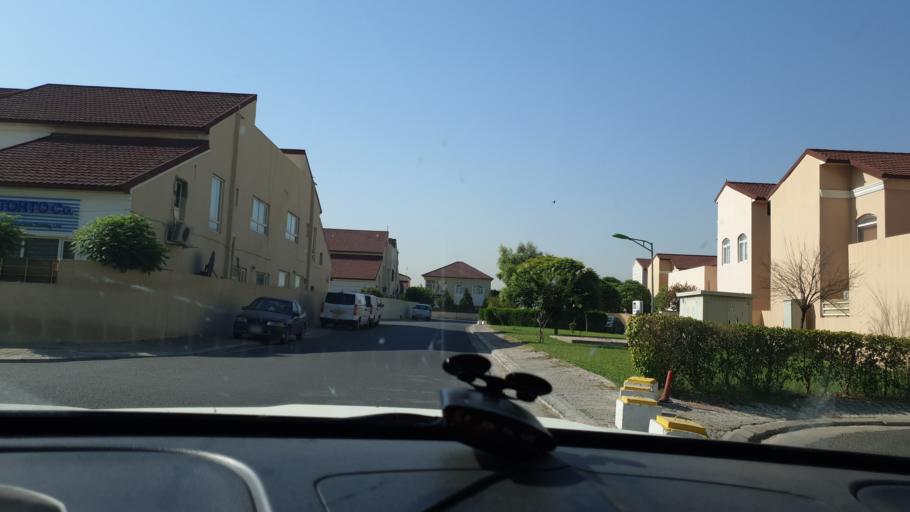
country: IQ
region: Arbil
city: Erbil
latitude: 36.1873
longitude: 43.9680
